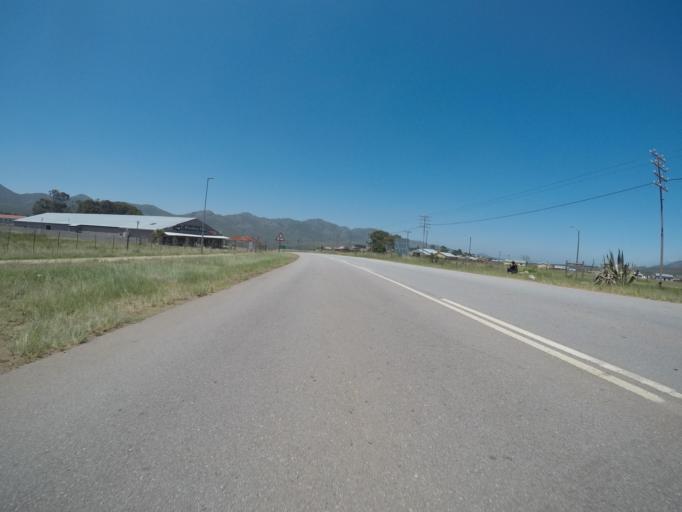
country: ZA
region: Eastern Cape
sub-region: Cacadu District Municipality
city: Kareedouw
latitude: -33.9521
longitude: 24.2992
